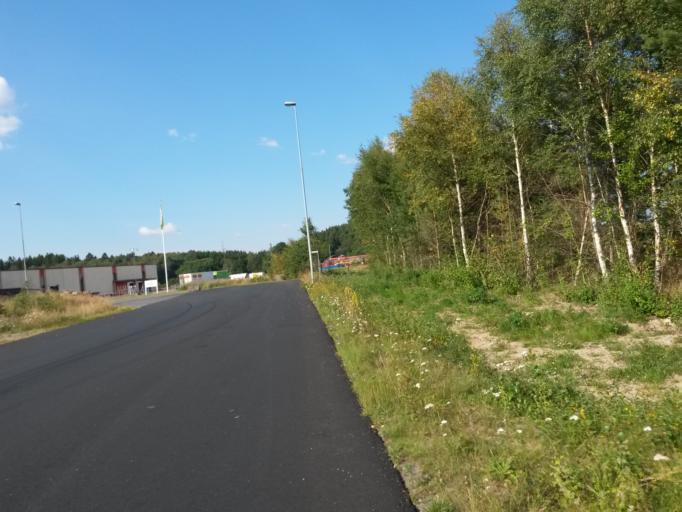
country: SE
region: Vaestra Goetaland
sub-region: Vargarda Kommun
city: Vargarda
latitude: 58.0427
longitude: 12.8071
